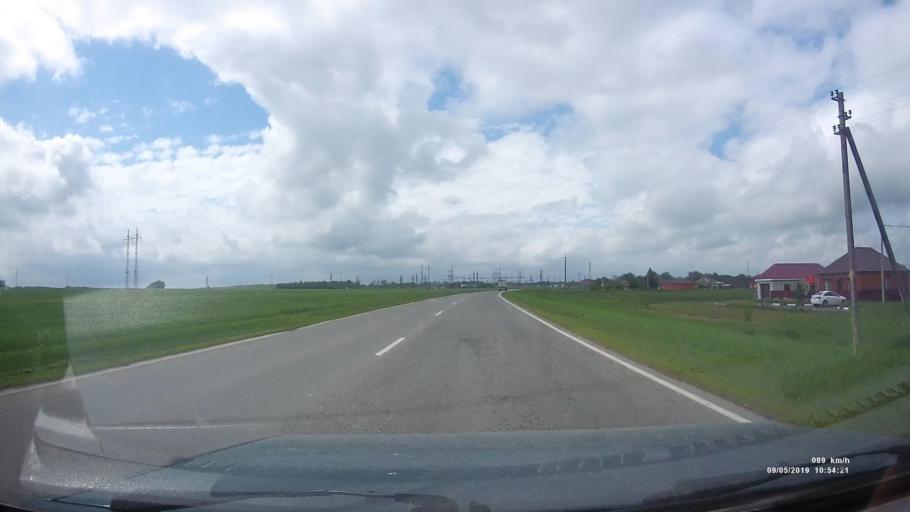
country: RU
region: Rostov
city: Peshkovo
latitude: 46.8785
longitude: 39.3316
